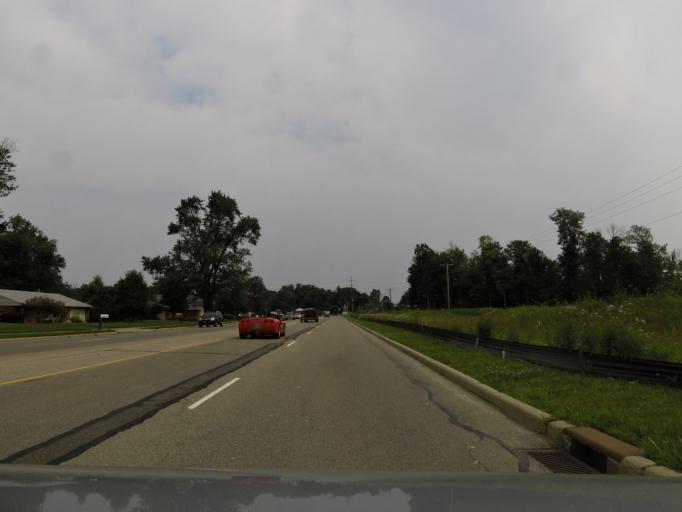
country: US
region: Ohio
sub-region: Greene County
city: Bellbrook
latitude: 39.6651
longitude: -84.1088
